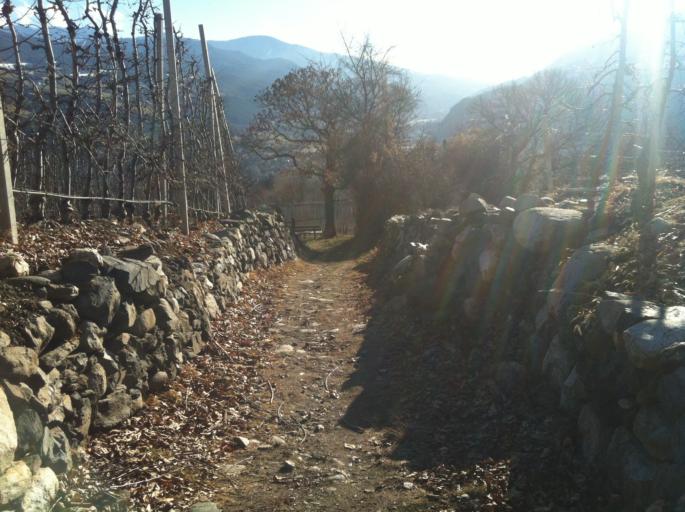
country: IT
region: Trentino-Alto Adige
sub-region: Bolzano
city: Bressanone
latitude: 46.7255
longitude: 11.6683
